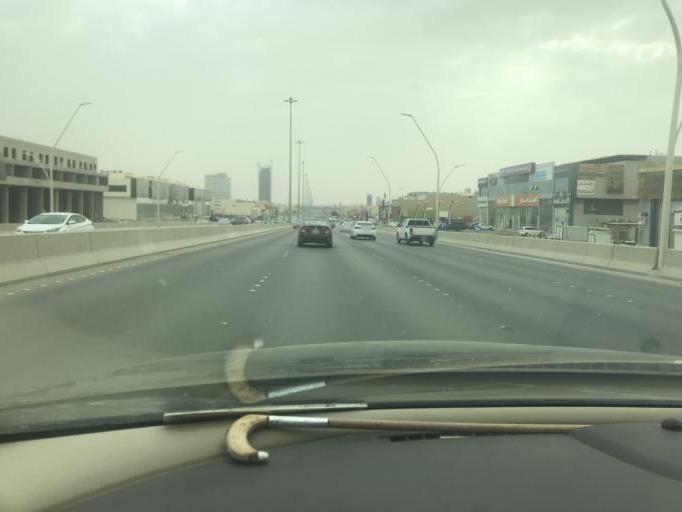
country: SA
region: Ar Riyad
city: Riyadh
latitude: 24.8181
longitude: 46.6406
